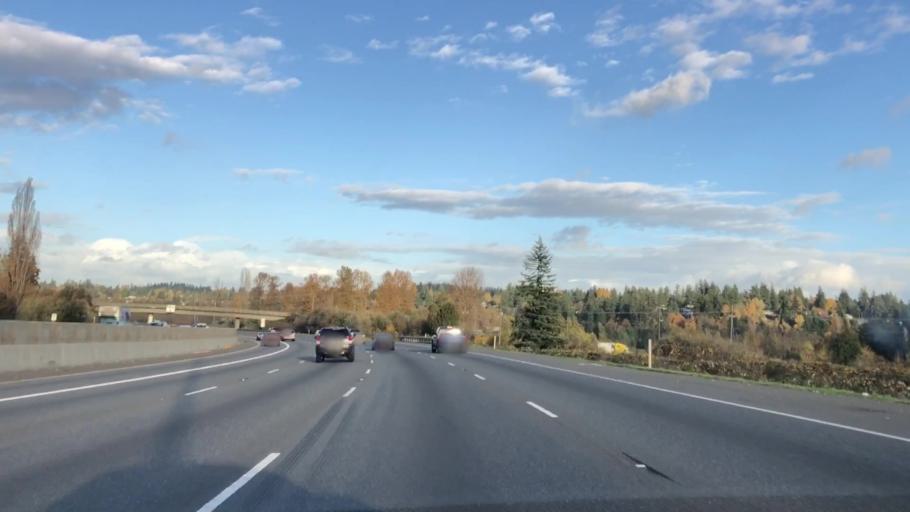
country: US
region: Washington
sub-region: Pierce County
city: Fife
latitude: 47.2420
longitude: -122.3398
